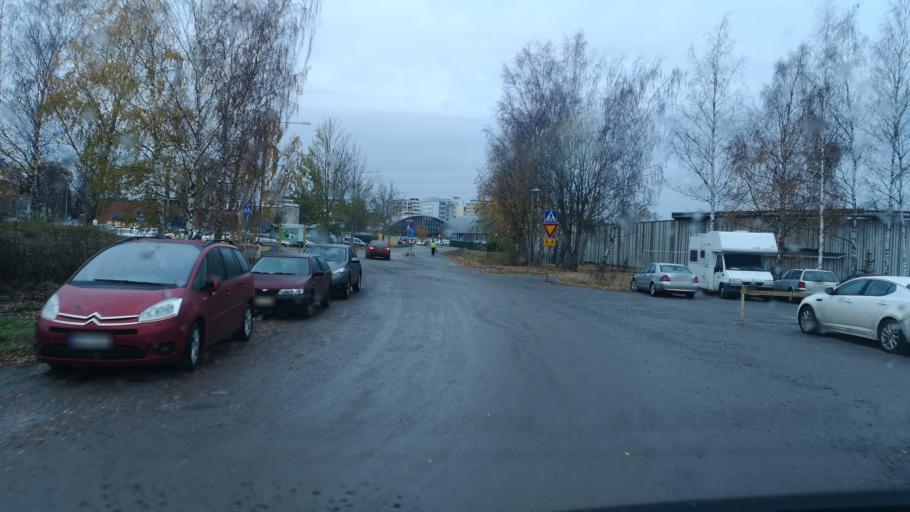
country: FI
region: Ostrobothnia
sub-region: Vaasa
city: Vaasa
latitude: 63.0836
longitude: 21.6202
